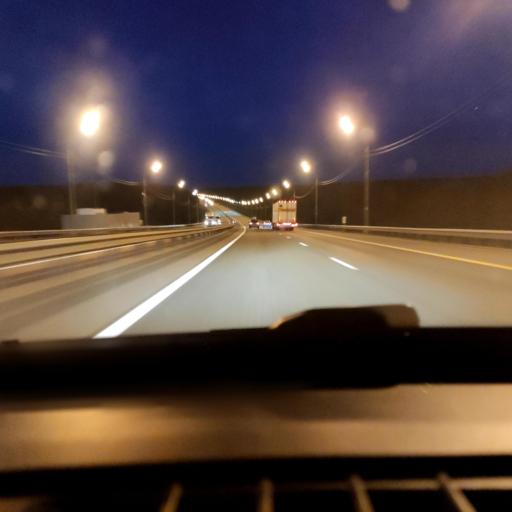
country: RU
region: Lipetsk
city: Khlevnoye
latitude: 52.2265
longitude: 39.1010
